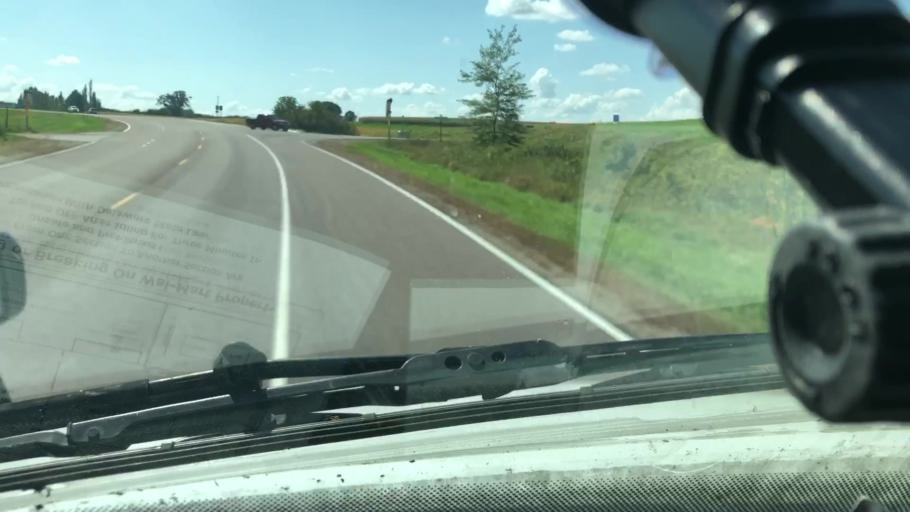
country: US
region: Minnesota
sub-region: Winona County
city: Winona
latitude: 43.9811
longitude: -91.6798
